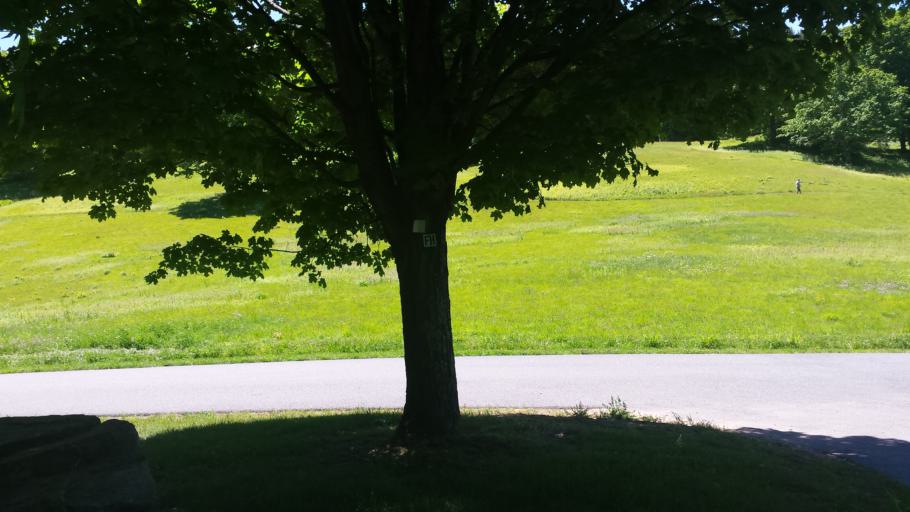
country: US
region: New York
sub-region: Westchester County
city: Pound Ridge
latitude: 41.2591
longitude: -73.5875
